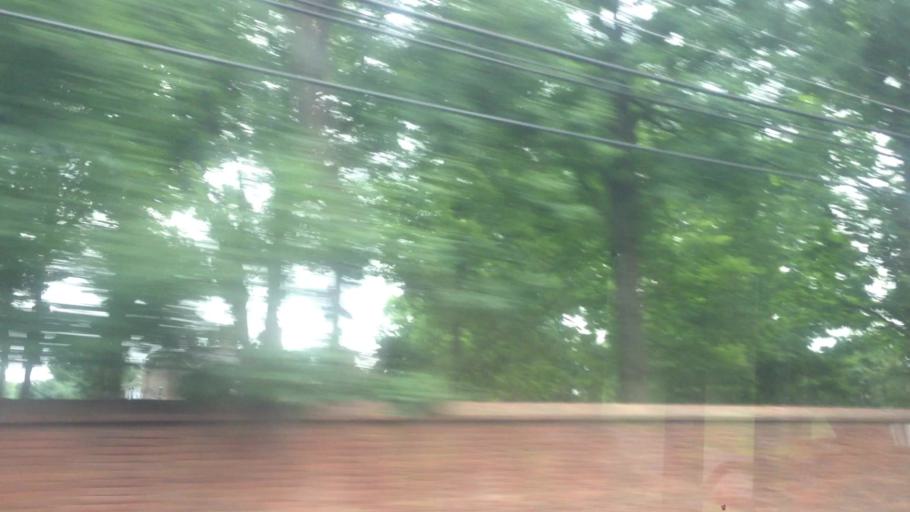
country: US
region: New York
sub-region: Dutchess County
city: Red Hook
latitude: 41.9973
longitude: -73.8825
